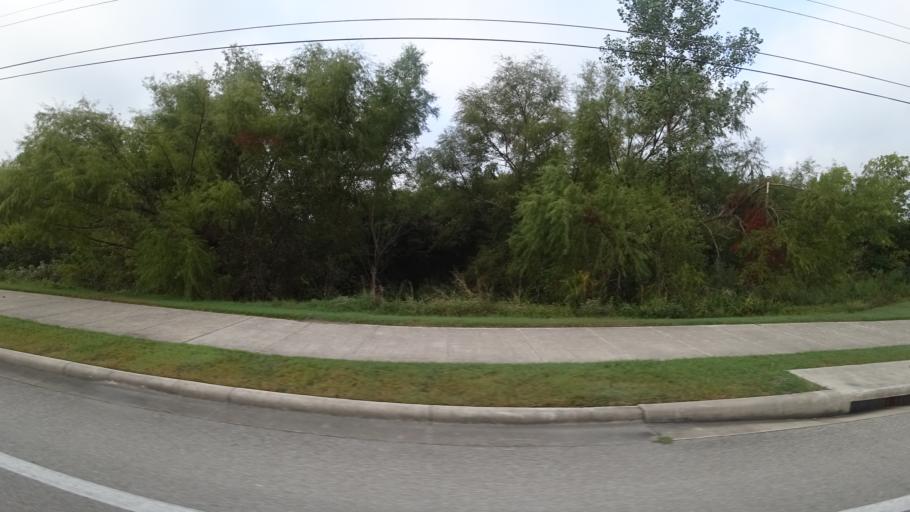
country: US
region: Texas
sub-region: Travis County
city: Pflugerville
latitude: 30.3698
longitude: -97.6539
